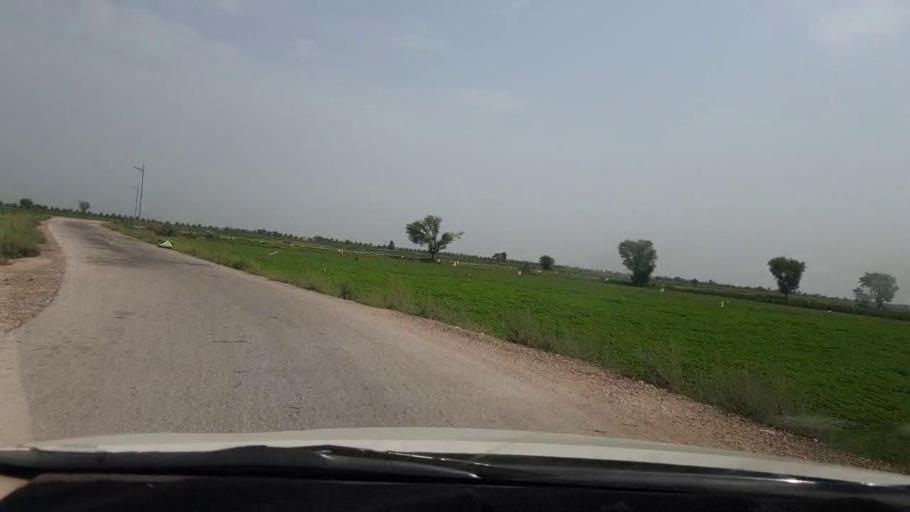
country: PK
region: Sindh
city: Rohri
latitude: 27.5374
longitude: 69.0042
